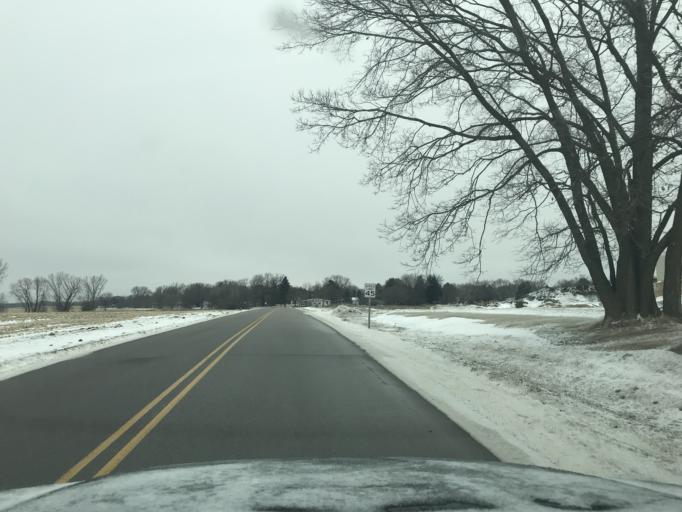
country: US
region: Wisconsin
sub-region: Dane County
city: Cottage Grove
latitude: 43.0904
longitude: -89.2352
